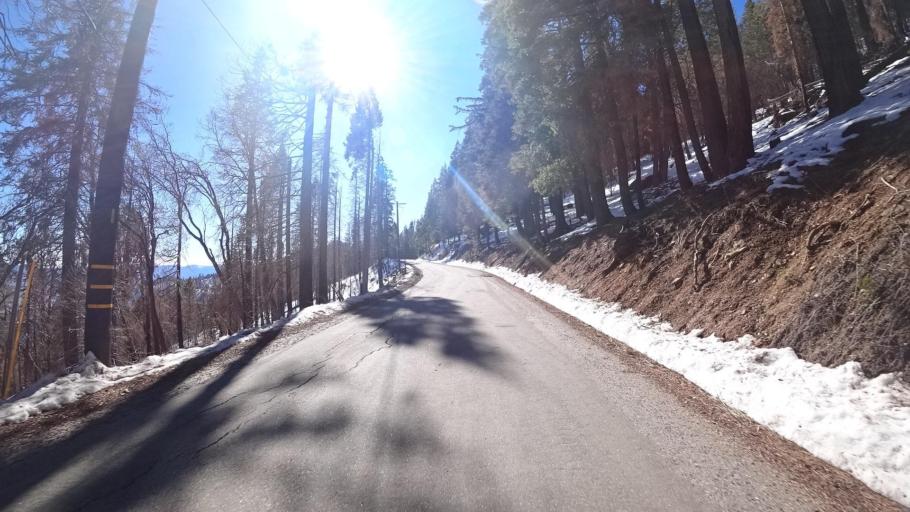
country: US
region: California
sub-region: Kern County
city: Alta Sierra
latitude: 35.7235
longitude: -118.5552
